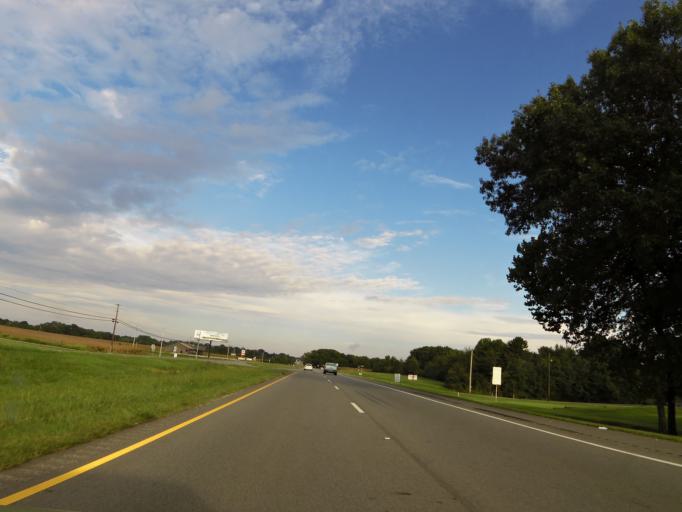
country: US
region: Alabama
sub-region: Lauderdale County
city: Rogersville
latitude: 34.8290
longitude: -87.3133
